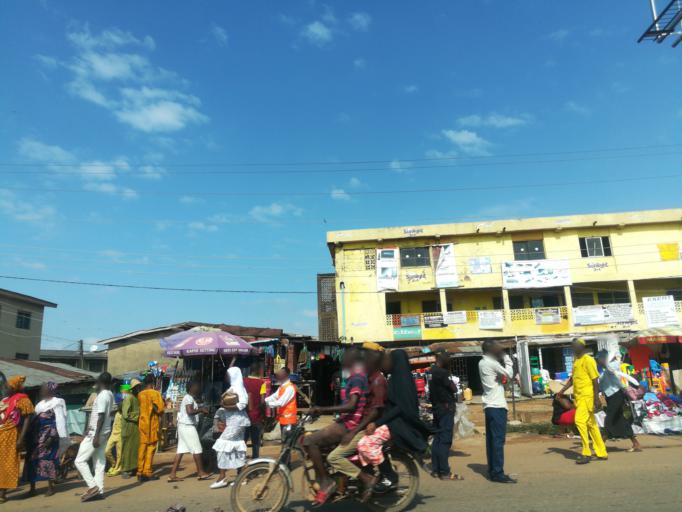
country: NG
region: Oyo
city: Ibadan
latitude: 7.4060
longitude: 3.9450
